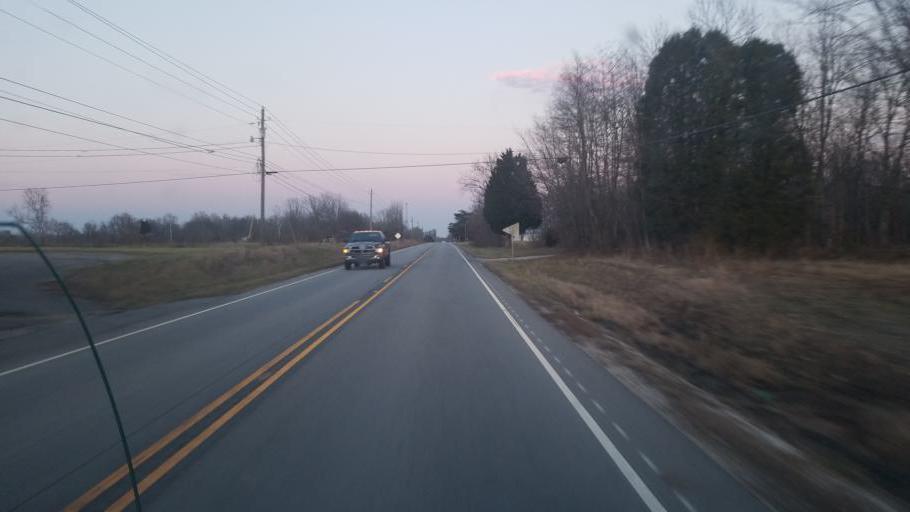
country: US
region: Indiana
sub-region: Lawrence County
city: Bedford
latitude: 38.8761
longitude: -86.2809
